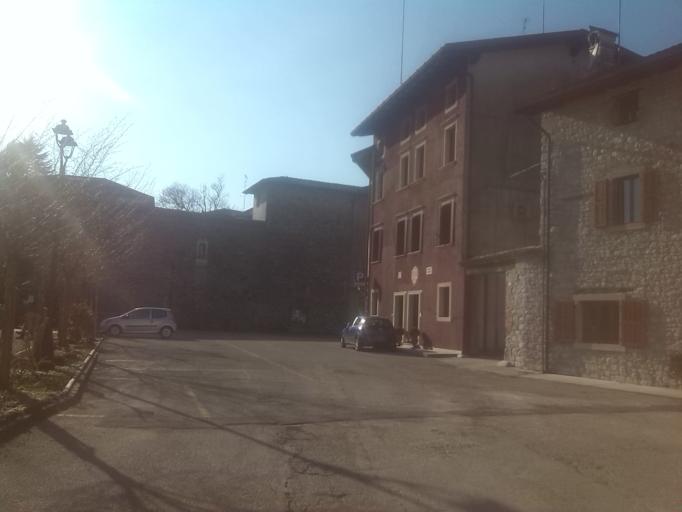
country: IT
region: Friuli Venezia Giulia
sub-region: Provincia di Udine
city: Cividale del Friuli
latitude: 46.0942
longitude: 13.4341
